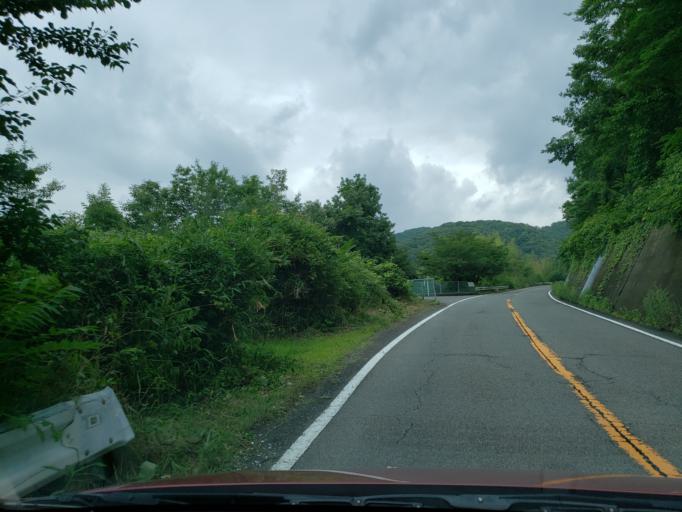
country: JP
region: Tokushima
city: Kamojimacho-jogejima
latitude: 34.1050
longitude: 134.2778
